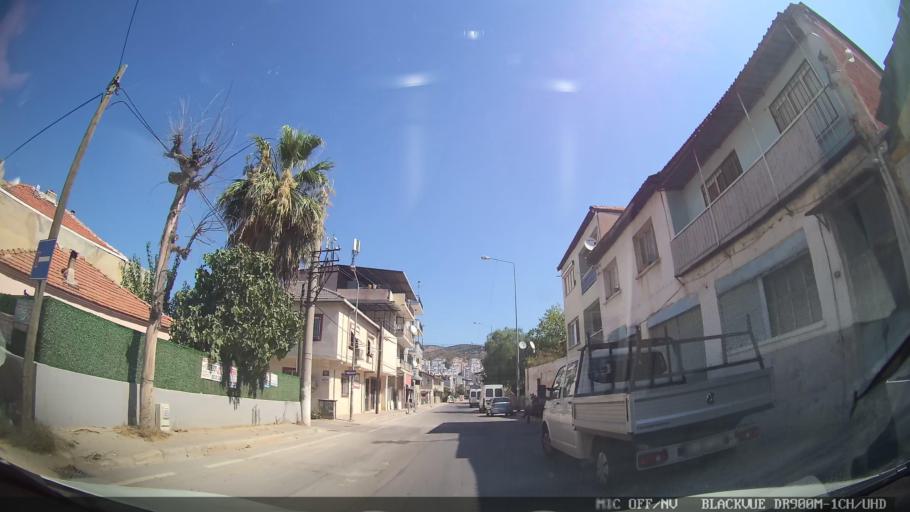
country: TR
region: Izmir
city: Karsiyaka
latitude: 38.4948
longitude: 27.0659
